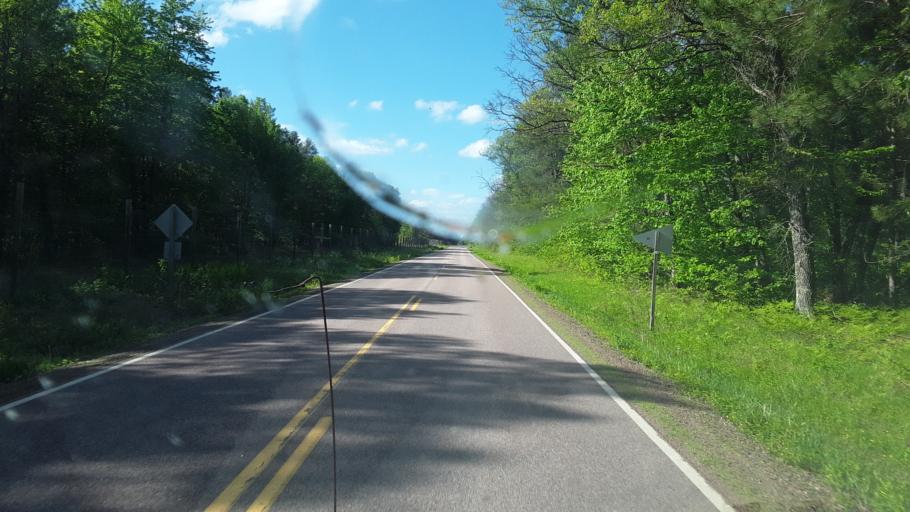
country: US
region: Wisconsin
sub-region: Wood County
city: Nekoosa
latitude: 44.3571
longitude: -90.1304
